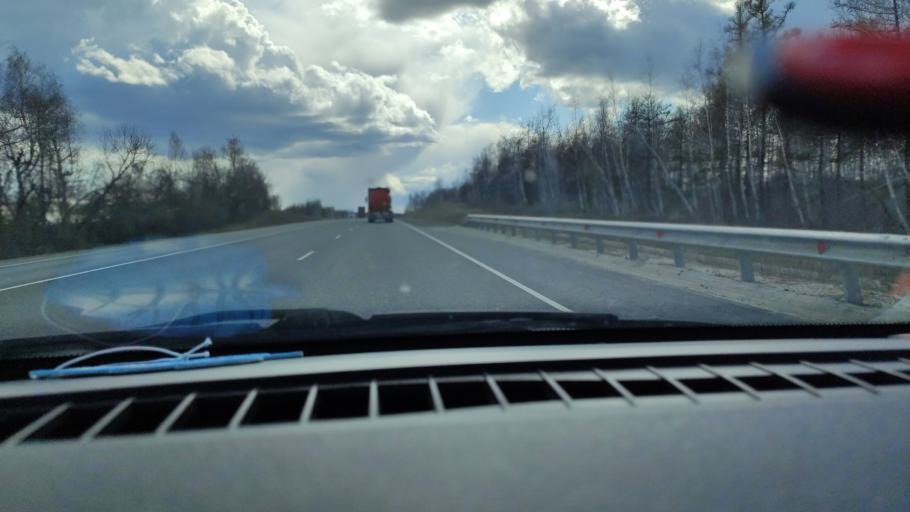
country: RU
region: Saratov
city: Khvalynsk
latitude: 52.5580
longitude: 48.0850
